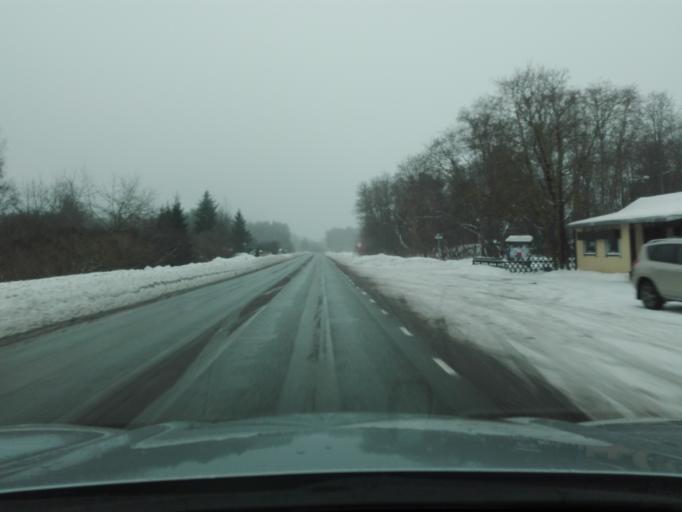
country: EE
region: Harju
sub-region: Kiili vald
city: Kiili
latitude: 59.3377
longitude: 24.7739
